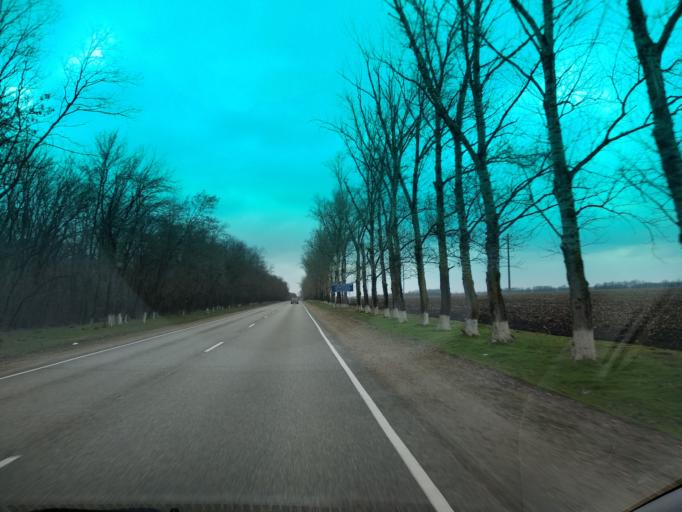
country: RU
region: Krasnodarskiy
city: Novorozhdestvenskaya
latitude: 45.7775
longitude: 39.9642
